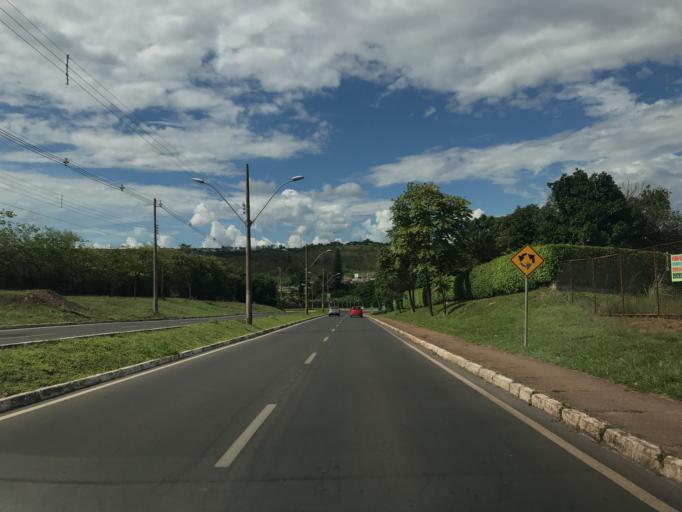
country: BR
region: Federal District
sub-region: Brasilia
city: Brasilia
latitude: -15.7194
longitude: -47.8791
